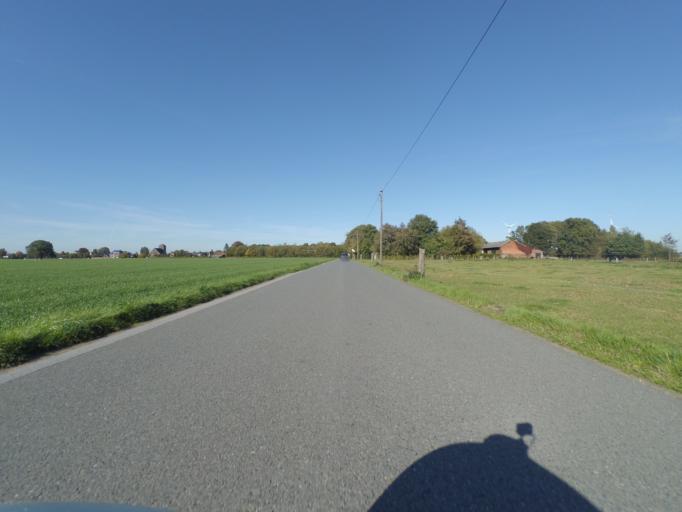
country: DE
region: North Rhine-Westphalia
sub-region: Regierungsbezirk Dusseldorf
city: Bocholt
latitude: 51.8589
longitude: 6.5660
